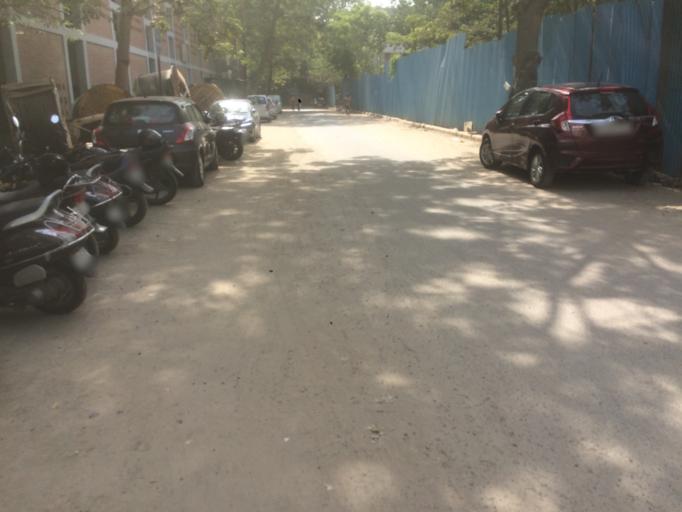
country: IN
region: NCT
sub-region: New Delhi
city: New Delhi
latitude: 28.6350
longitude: 77.2107
